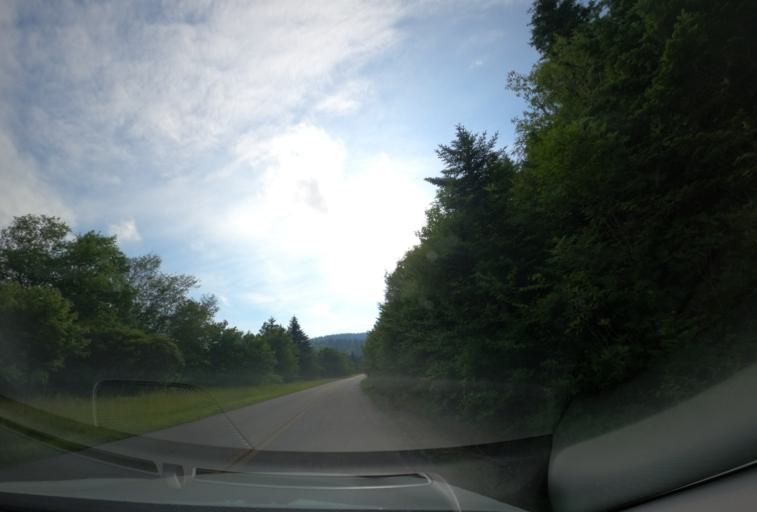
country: US
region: North Carolina
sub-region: Transylvania County
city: Brevard
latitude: 35.3051
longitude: -82.9016
